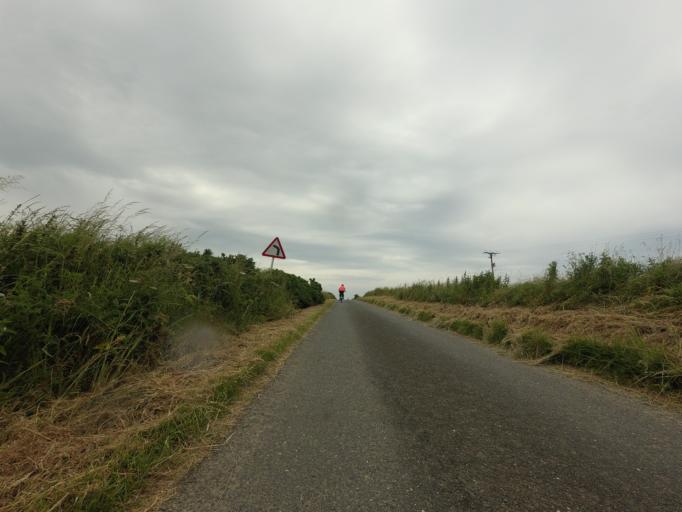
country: GB
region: Scotland
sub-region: Aberdeenshire
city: Portsoy
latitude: 57.6789
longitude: -2.6743
